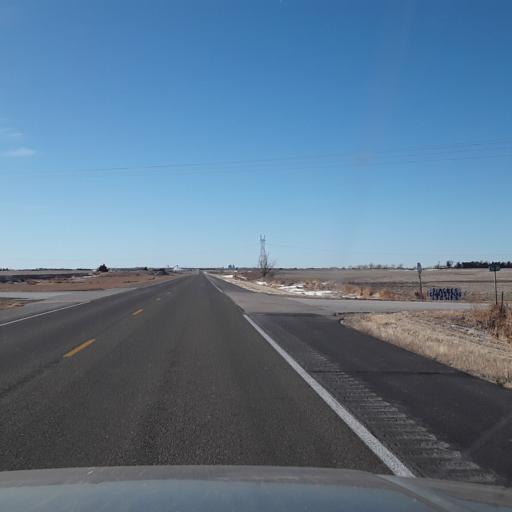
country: US
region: Nebraska
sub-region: Kearney County
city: Minden
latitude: 40.5322
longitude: -98.8751
